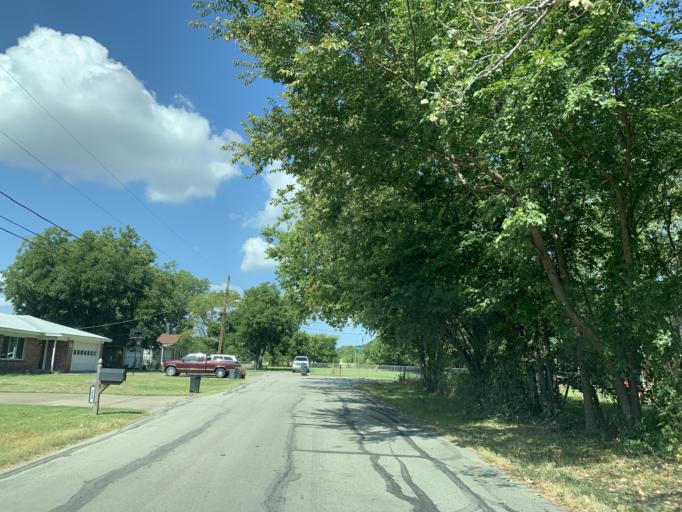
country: US
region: Texas
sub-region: Tarrant County
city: Azle
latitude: 32.8803
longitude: -97.5396
